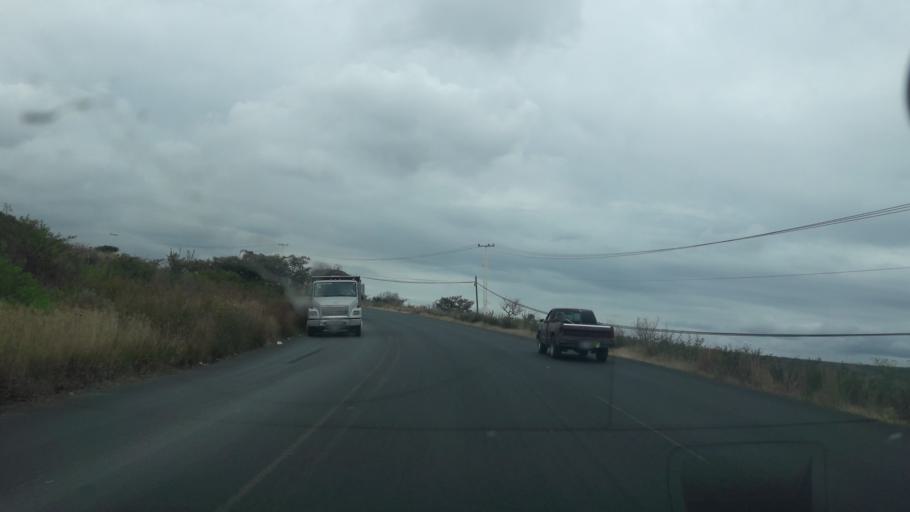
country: MX
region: Guanajuato
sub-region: Leon
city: La Ermita
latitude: 21.1771
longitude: -101.7249
